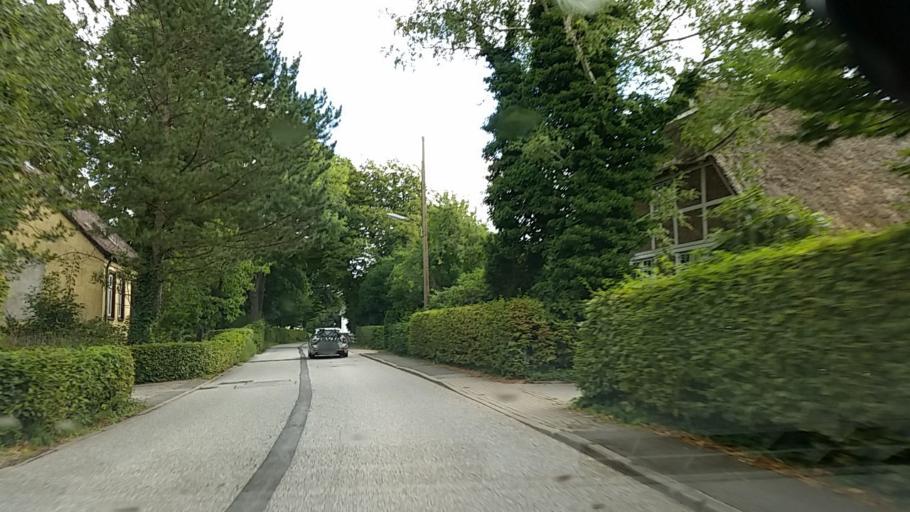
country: DE
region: Schleswig-Holstein
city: Bornsen
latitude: 53.4661
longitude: 10.2590
